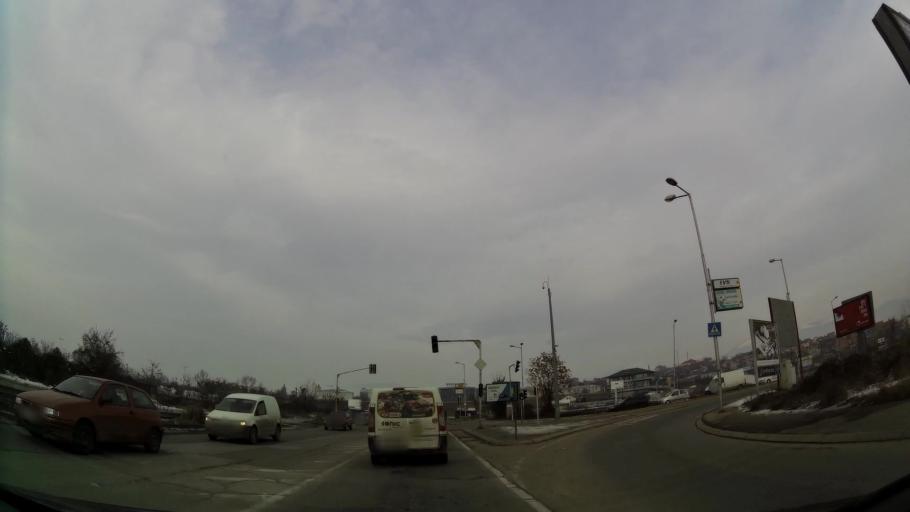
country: MK
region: Suto Orizari
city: Suto Orizare
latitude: 42.0248
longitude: 21.4090
